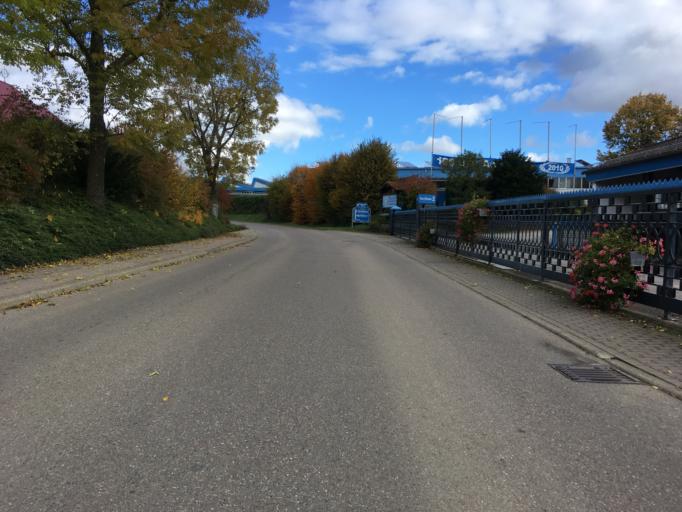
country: DE
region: Baden-Wuerttemberg
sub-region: Regierungsbezirk Stuttgart
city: Untermunkheim
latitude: 49.1848
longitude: 9.7253
